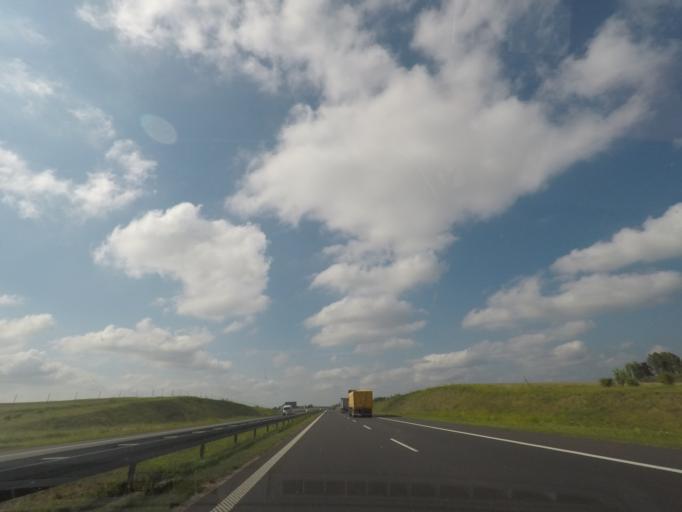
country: PL
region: Kujawsko-Pomorskie
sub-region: Powiat swiecki
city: Warlubie
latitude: 53.5931
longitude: 18.6144
